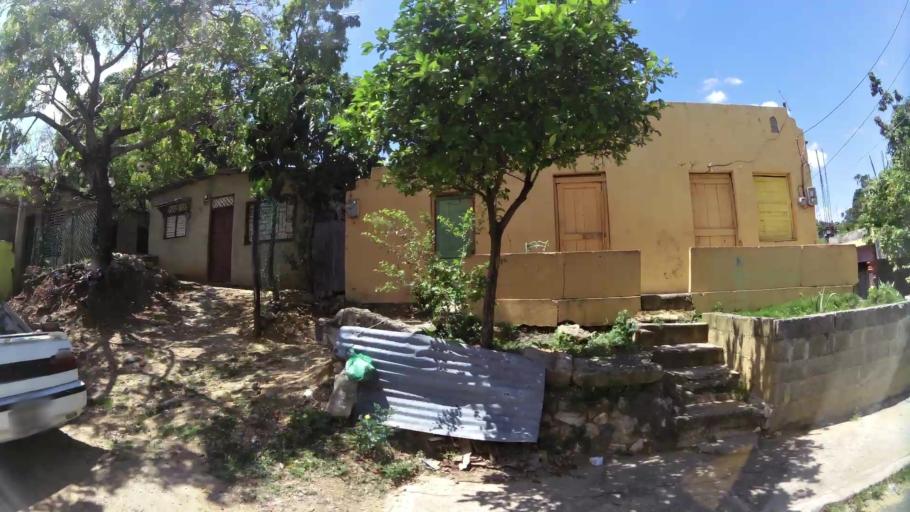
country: DO
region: San Cristobal
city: San Cristobal
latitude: 18.4048
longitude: -70.1143
